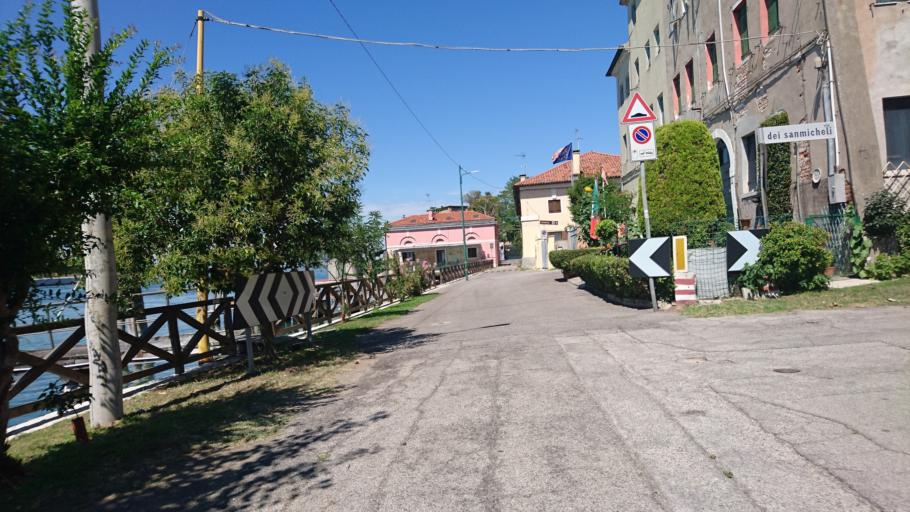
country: IT
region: Veneto
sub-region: Provincia di Venezia
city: Lido
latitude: 45.4314
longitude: 12.3833
